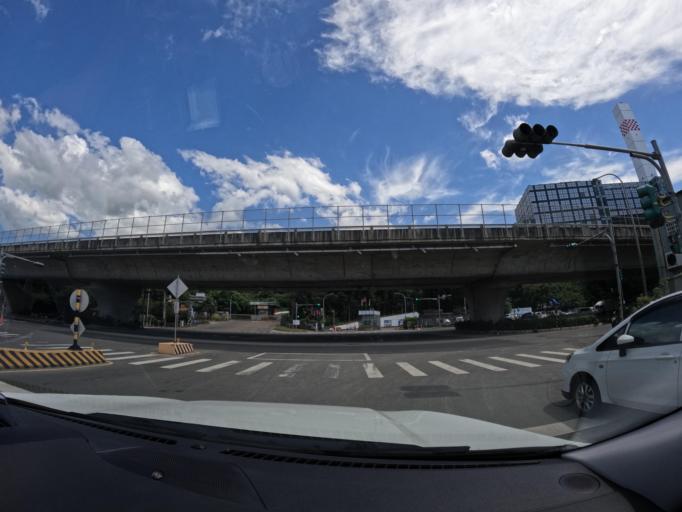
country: TW
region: Taiwan
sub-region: Taoyuan
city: Taoyuan
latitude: 25.1366
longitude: 121.3683
